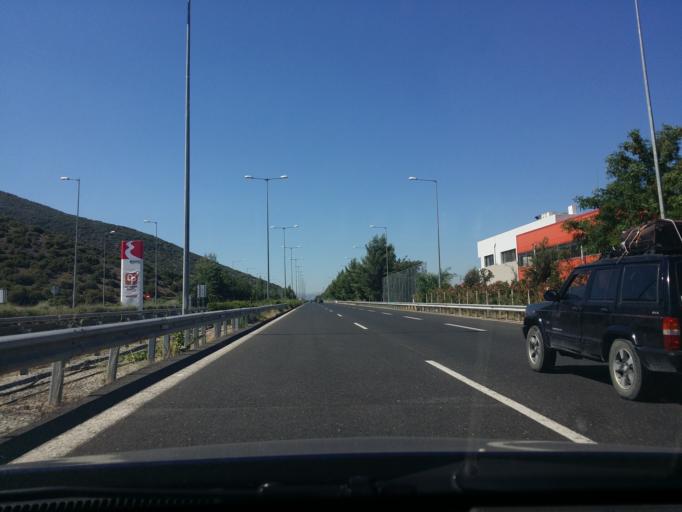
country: GR
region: Peloponnese
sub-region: Nomos Arkadias
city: Tripoli
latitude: 37.5798
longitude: 22.4313
